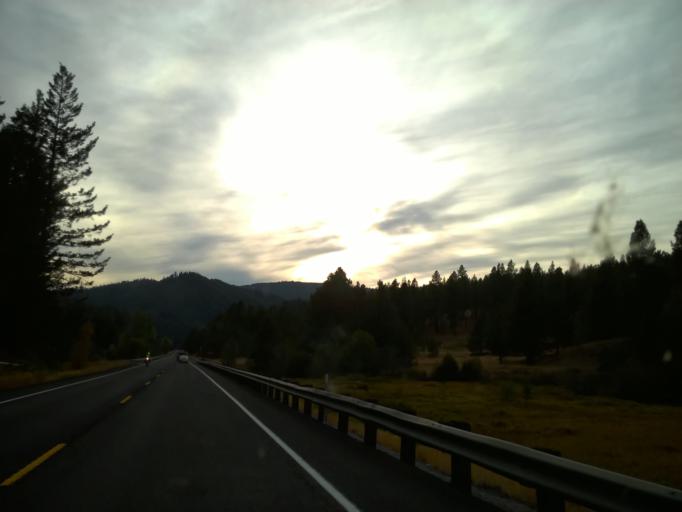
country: US
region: Washington
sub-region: Chelan County
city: Leavenworth
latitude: 47.3258
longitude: -120.6718
